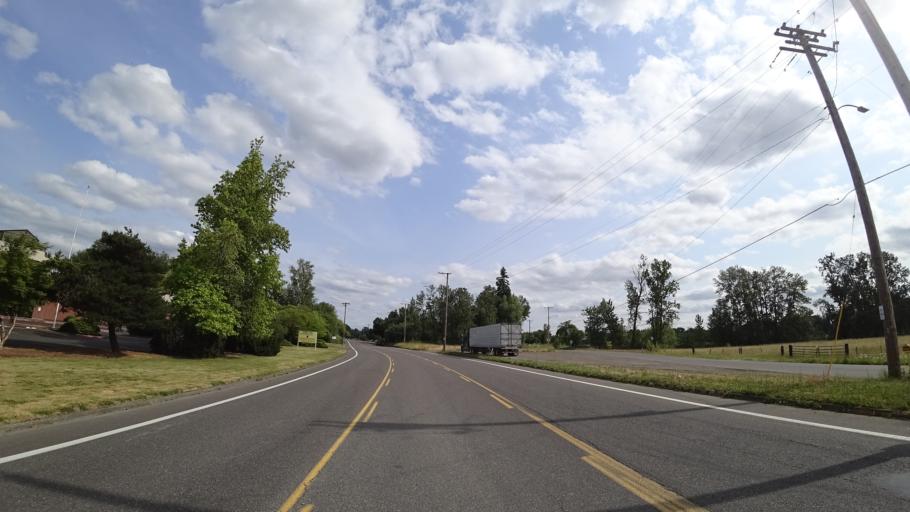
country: US
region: Washington
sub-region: Clark County
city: Vancouver
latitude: 45.5953
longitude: -122.6355
